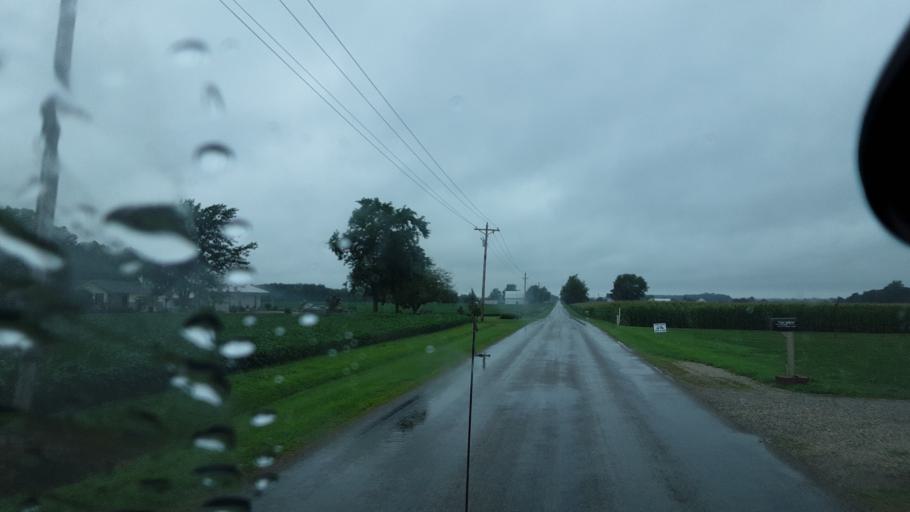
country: US
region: Indiana
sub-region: Adams County
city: Berne
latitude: 40.7228
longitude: -84.8535
